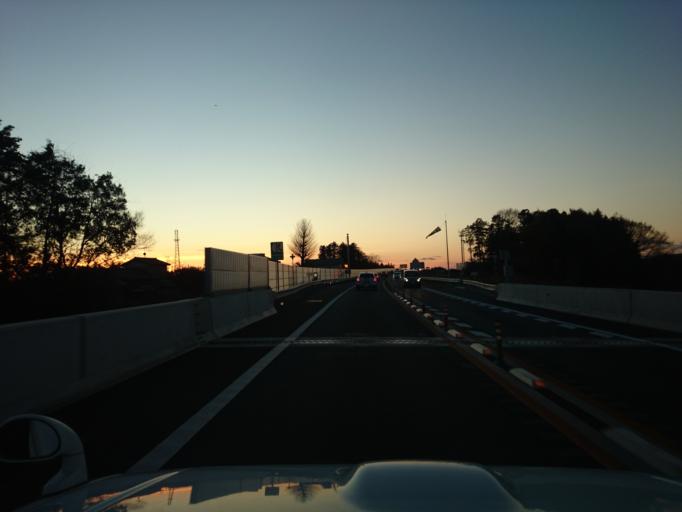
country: JP
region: Ibaraki
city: Ishige
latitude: 36.0734
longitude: 139.9667
